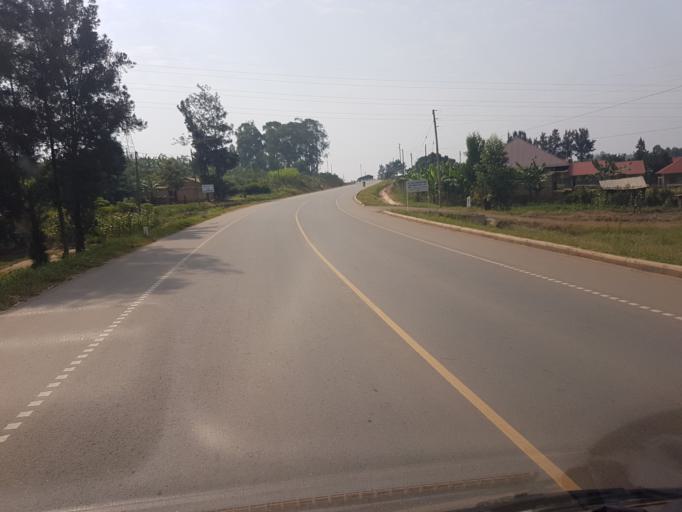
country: UG
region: Western Region
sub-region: Mbarara District
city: Bwizibwera
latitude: -0.6365
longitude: 30.6074
